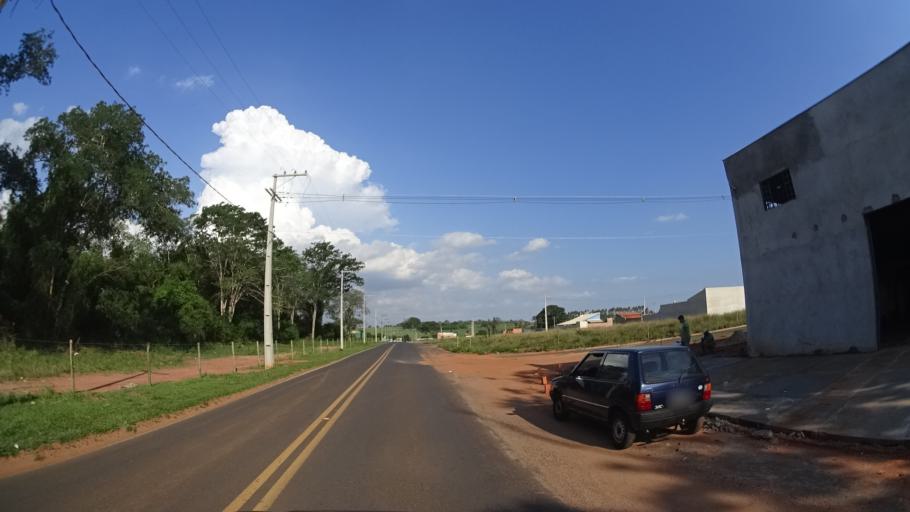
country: BR
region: Sao Paulo
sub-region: Urupes
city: Urupes
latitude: -21.3633
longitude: -49.4797
